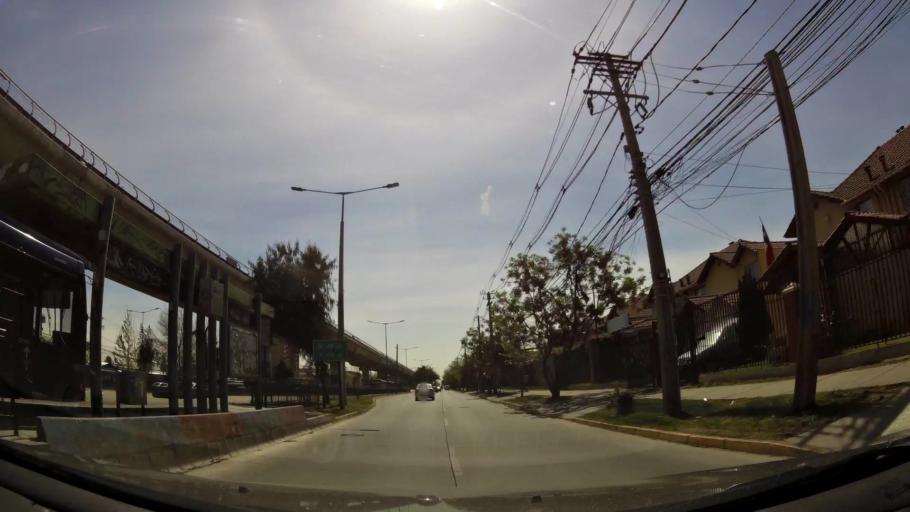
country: CL
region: Santiago Metropolitan
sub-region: Provincia de Cordillera
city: Puente Alto
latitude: -33.5888
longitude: -70.5798
